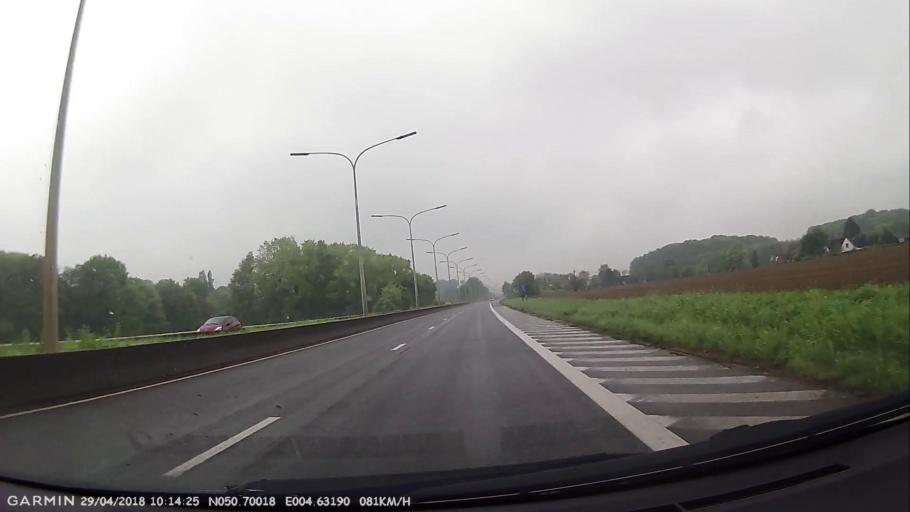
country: BE
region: Wallonia
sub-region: Province du Brabant Wallon
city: Wavre
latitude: 50.7000
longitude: 4.6316
